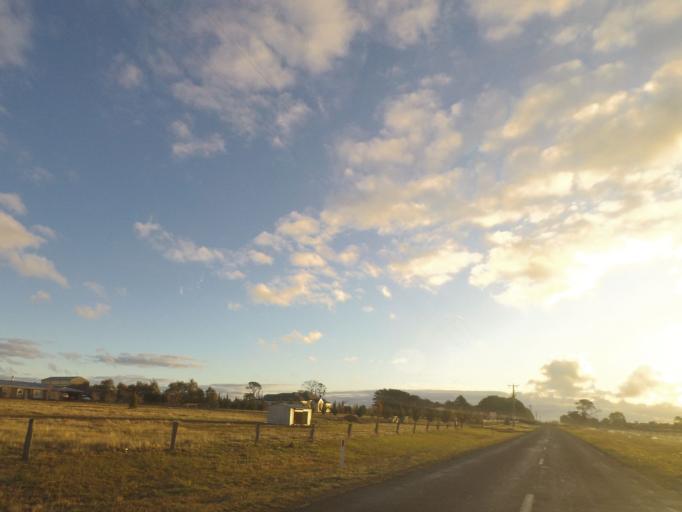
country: AU
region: Victoria
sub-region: Hume
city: Sunbury
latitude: -37.2861
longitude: 144.5114
